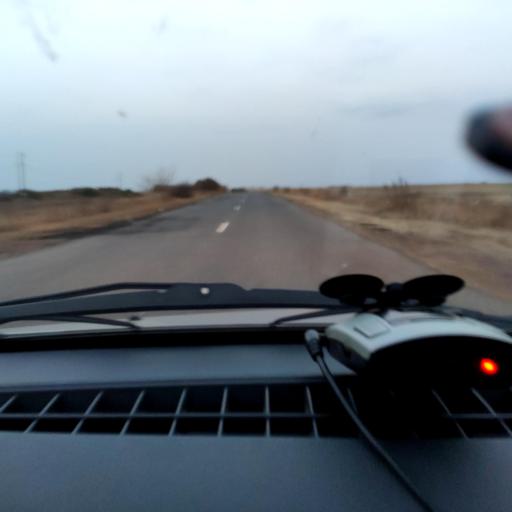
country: RU
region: Voronezj
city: Uryv-Pokrovka
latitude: 51.2407
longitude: 38.9715
